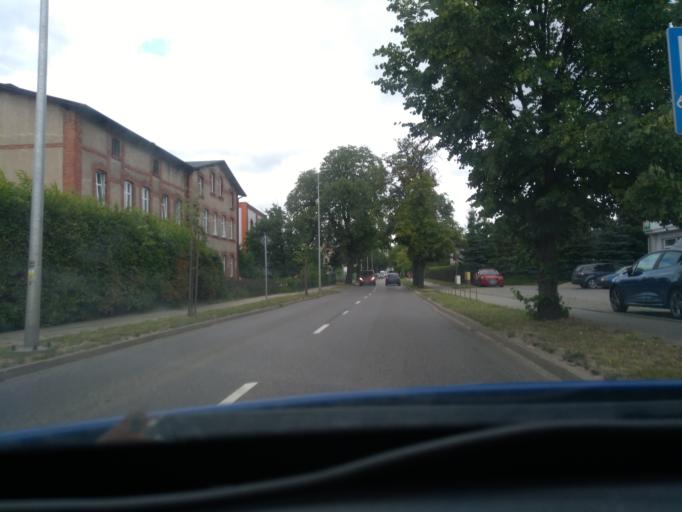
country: PL
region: Pomeranian Voivodeship
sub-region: Powiat kartuski
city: Kartuzy
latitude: 54.3268
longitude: 18.2042
